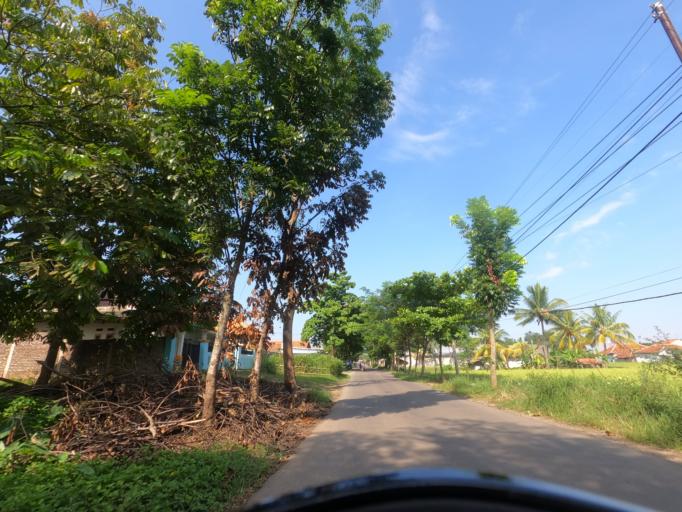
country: ID
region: West Java
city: Lembang
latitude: -6.5782
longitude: 107.7882
